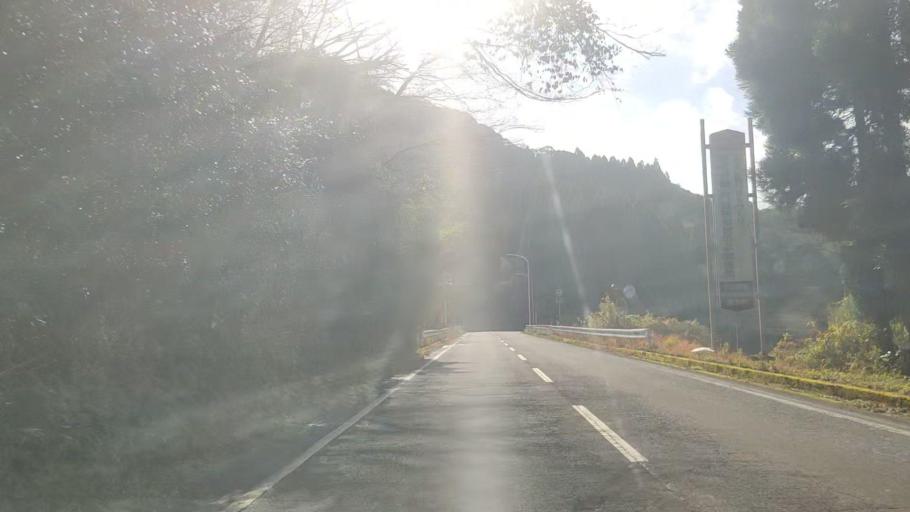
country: JP
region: Kagoshima
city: Okuchi-shinohara
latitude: 31.9781
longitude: 130.7419
